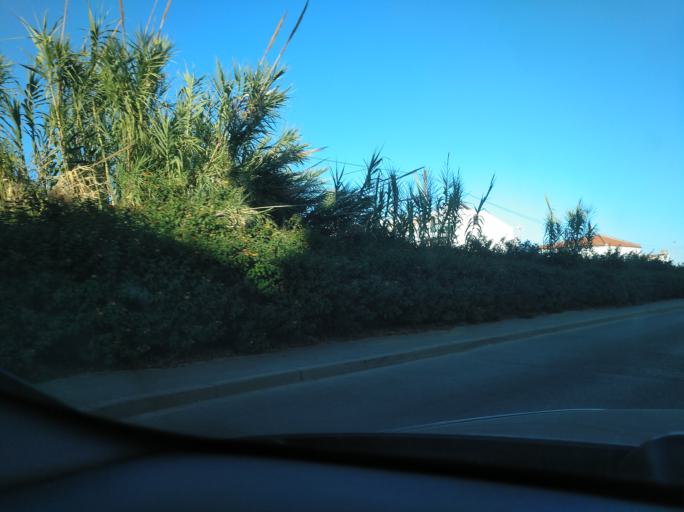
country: PT
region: Faro
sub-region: Vila Real de Santo Antonio
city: Monte Gordo
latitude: 37.1668
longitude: -7.5225
